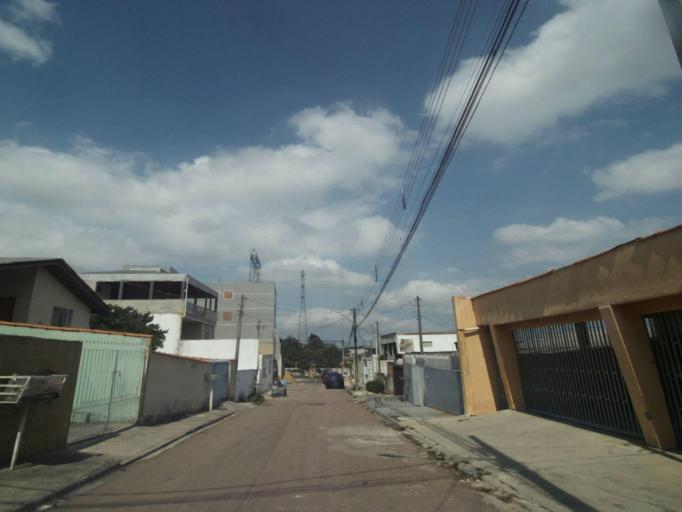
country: BR
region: Parana
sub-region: Curitiba
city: Curitiba
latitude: -25.5019
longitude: -49.3438
